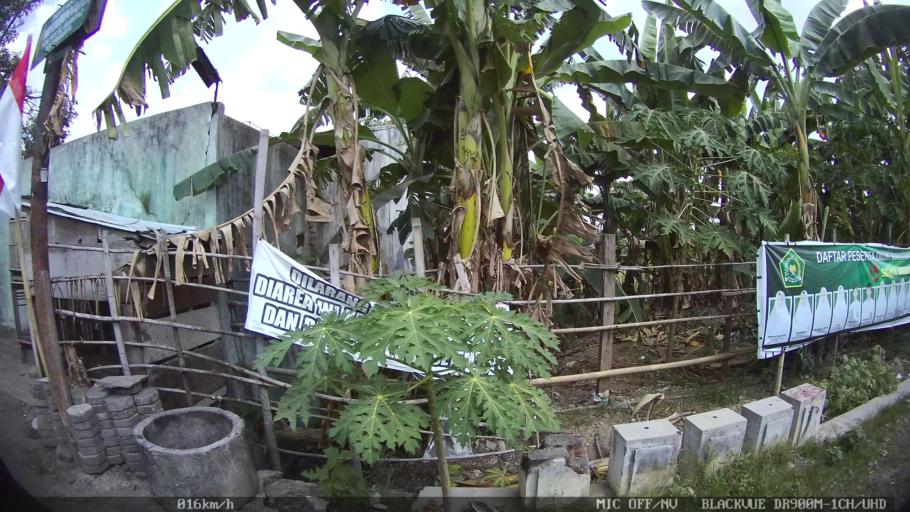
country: ID
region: Daerah Istimewa Yogyakarta
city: Depok
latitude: -7.8060
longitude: 110.4082
